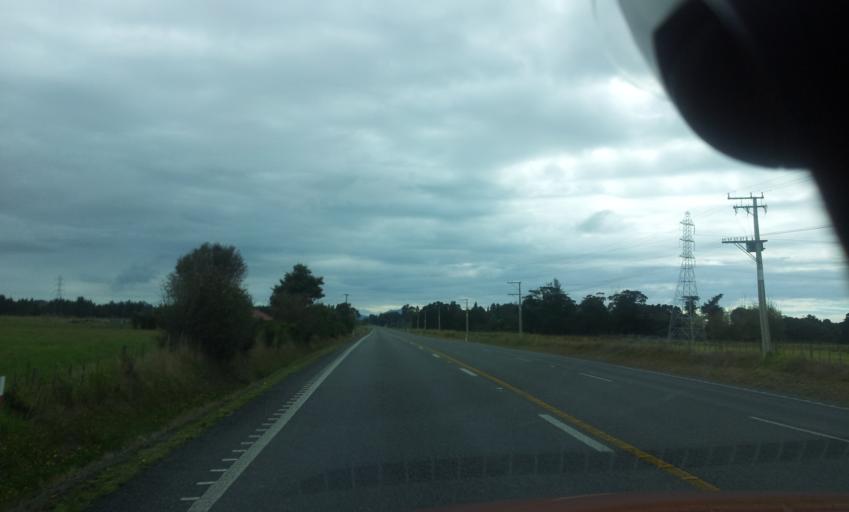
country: NZ
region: Northland
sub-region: Whangarei
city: Ruakaka
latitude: -35.9924
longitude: 174.4223
